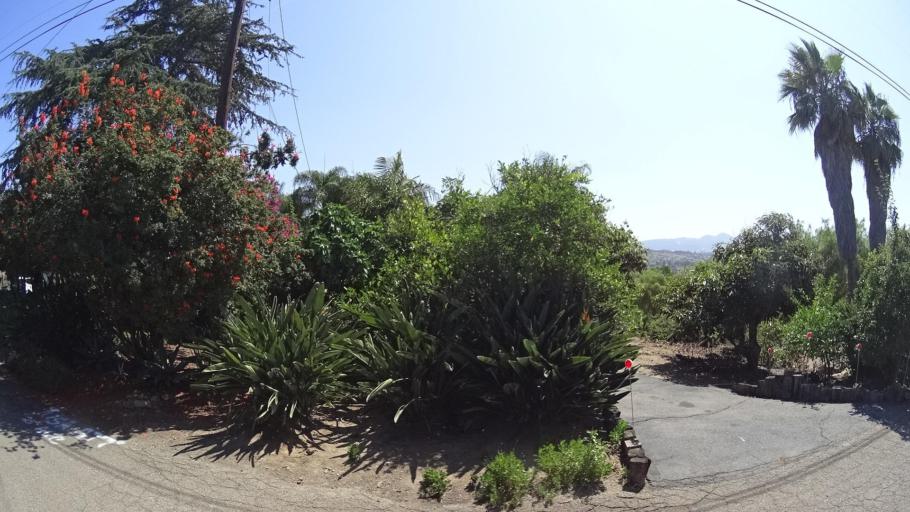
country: US
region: California
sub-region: San Diego County
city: San Marcos
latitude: 33.1693
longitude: -117.1940
